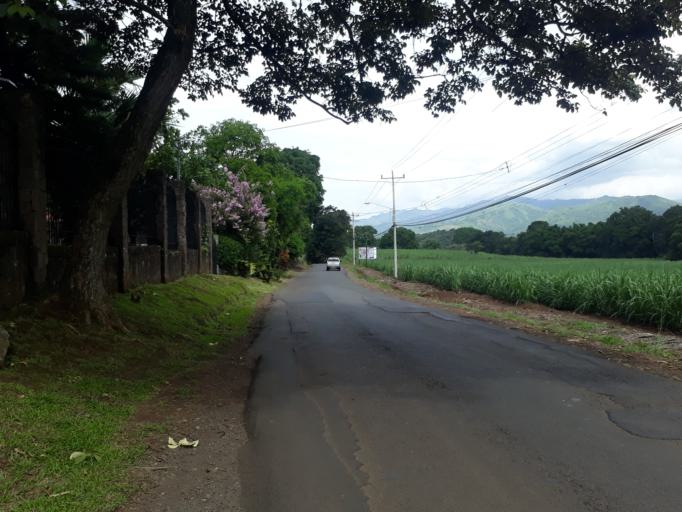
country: CR
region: Alajuela
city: Carrillos
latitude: 10.0242
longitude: -84.3339
